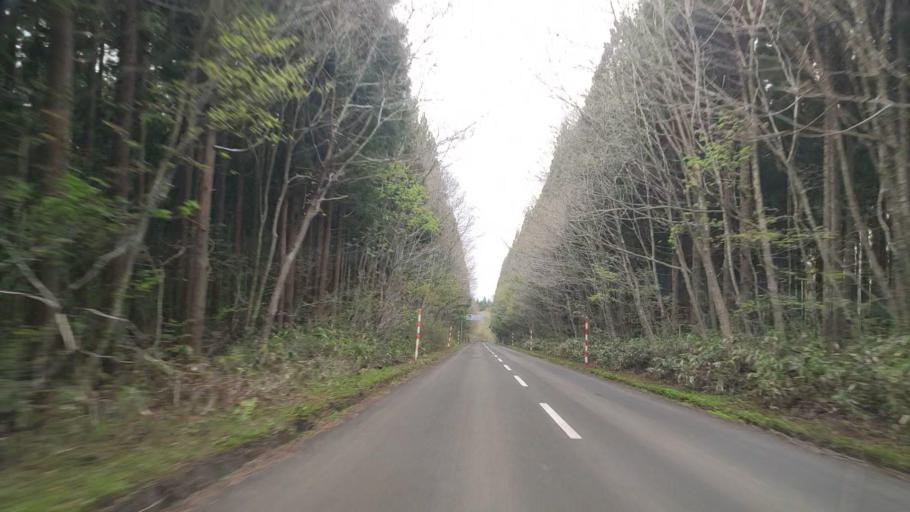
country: JP
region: Akita
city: Hanawa
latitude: 40.3872
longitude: 140.7931
